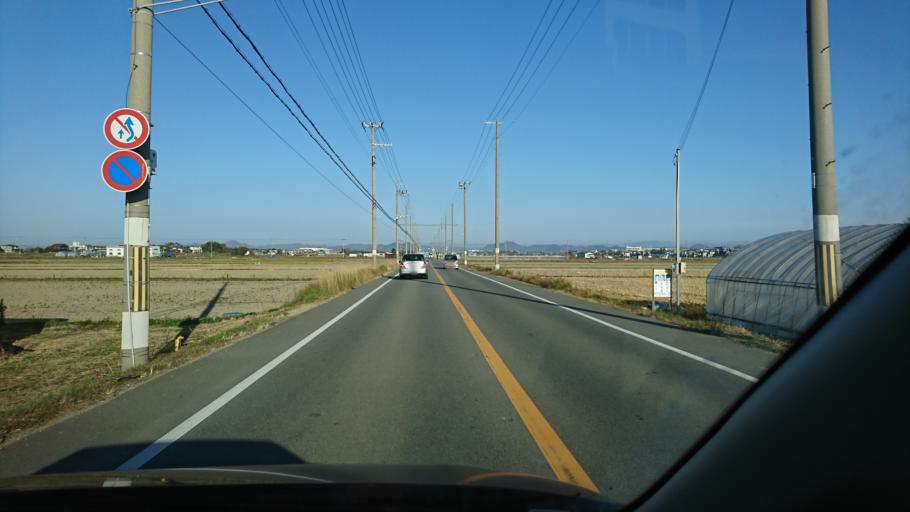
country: JP
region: Hyogo
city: Kakogawacho-honmachi
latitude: 34.7363
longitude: 134.9058
